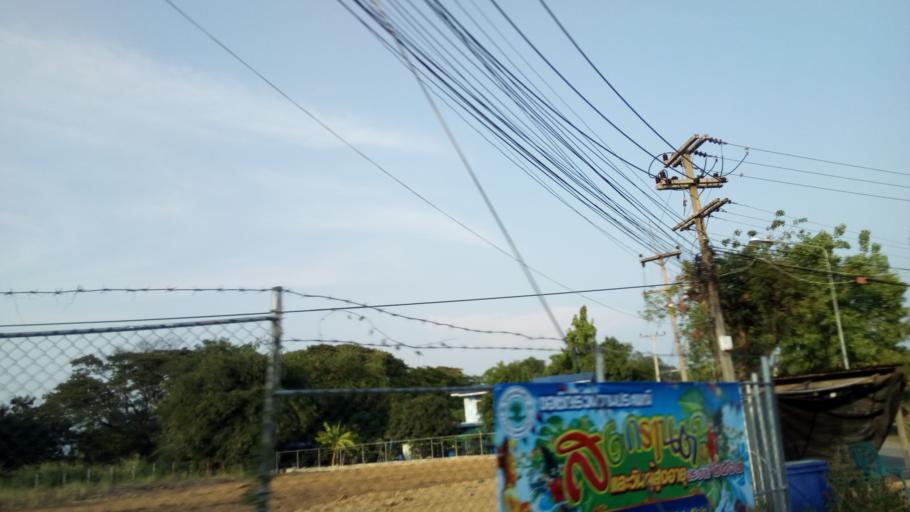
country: TH
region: Sara Buri
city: Nong Khae
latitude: 14.2758
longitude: 100.8219
